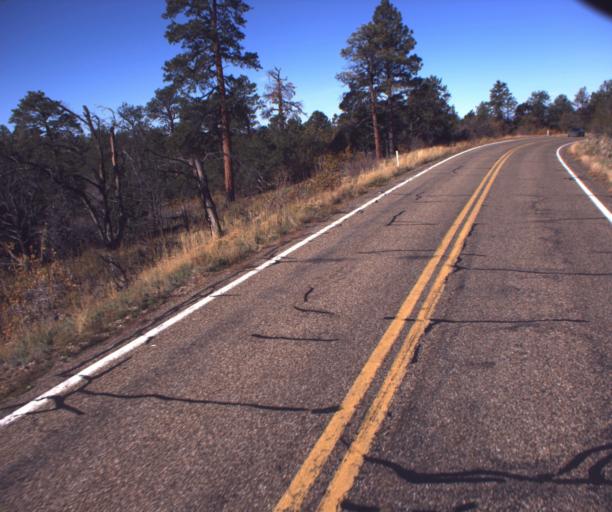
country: US
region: Arizona
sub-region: Coconino County
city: Fredonia
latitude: 36.7746
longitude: -112.2541
